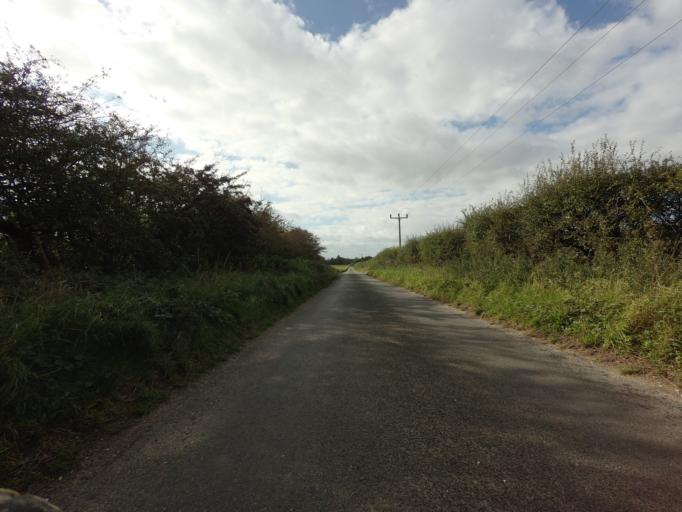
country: GB
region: England
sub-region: Norfolk
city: Hunstanton
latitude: 52.9350
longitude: 0.5744
